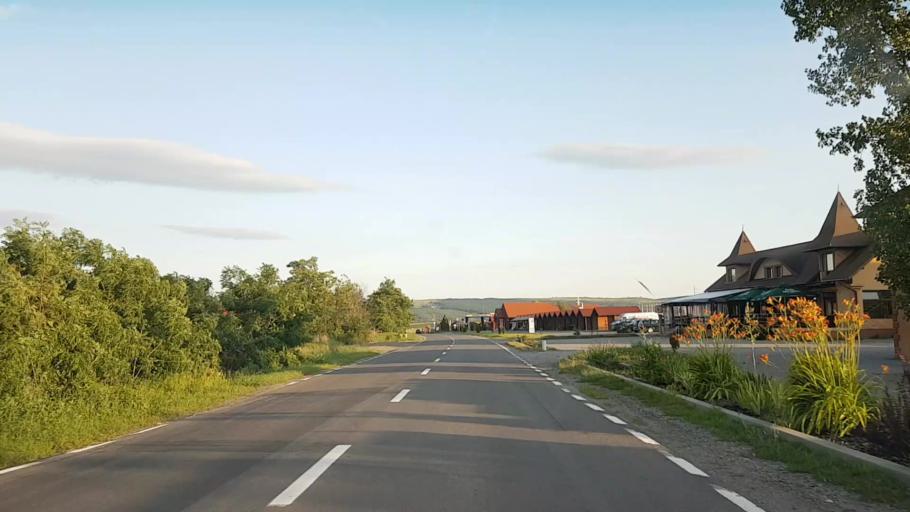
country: RO
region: Harghita
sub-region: Comuna Lupeni
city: Lupeni
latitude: 46.3787
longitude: 25.2193
